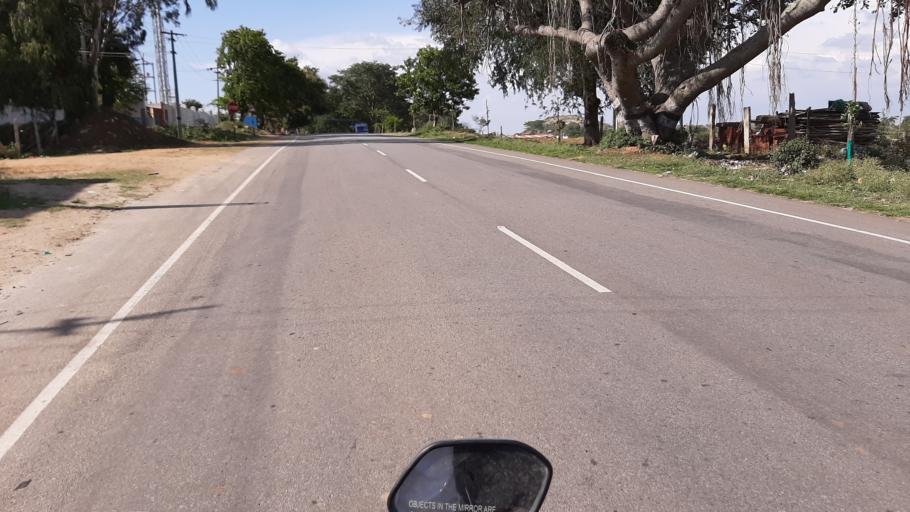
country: IN
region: Tamil Nadu
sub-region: Krishnagiri
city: Denkanikota
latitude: 12.5485
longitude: 77.7862
